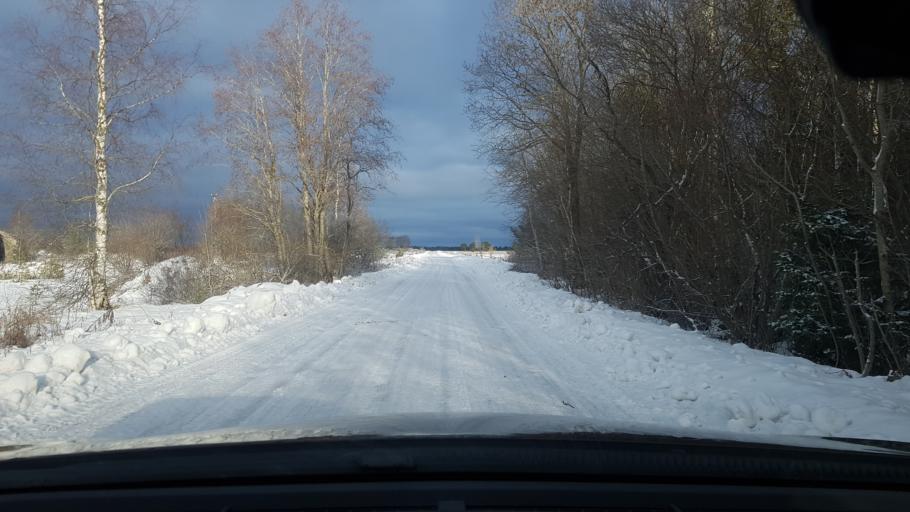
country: EE
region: Harju
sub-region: Keila linn
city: Keila
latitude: 59.3079
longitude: 24.2484
